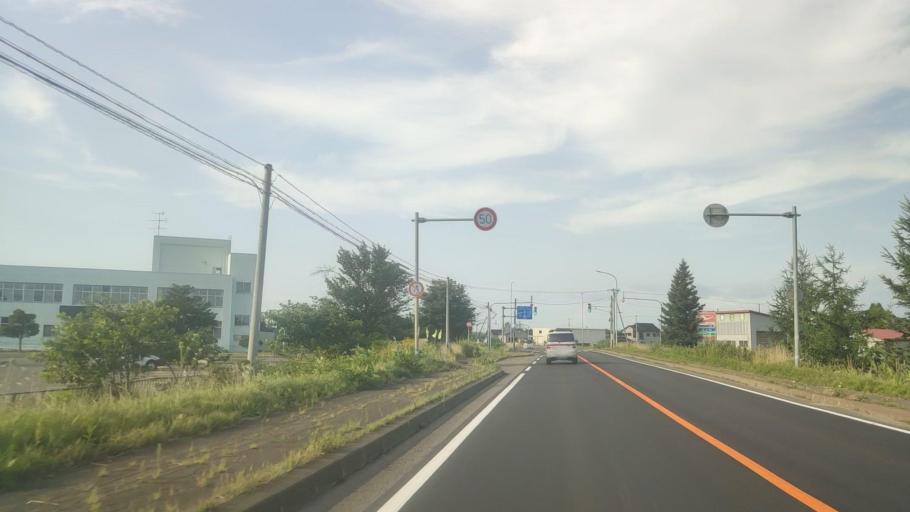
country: JP
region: Hokkaido
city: Iwamizawa
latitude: 43.0045
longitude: 141.7893
